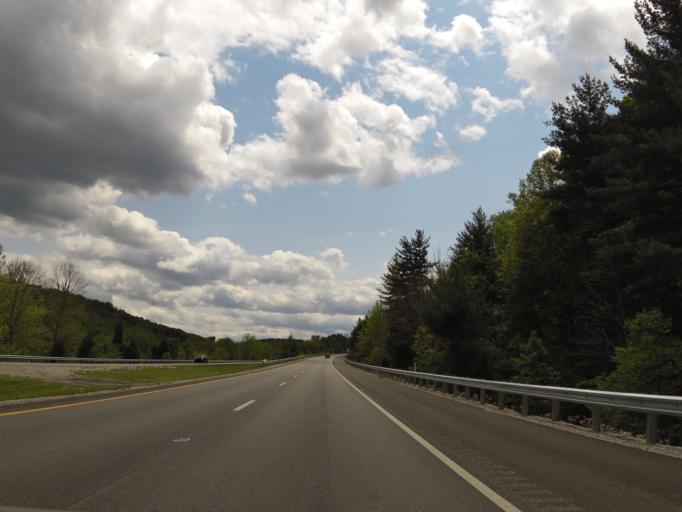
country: US
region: West Virginia
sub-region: Jackson County
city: Ripley
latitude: 38.6950
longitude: -81.6409
